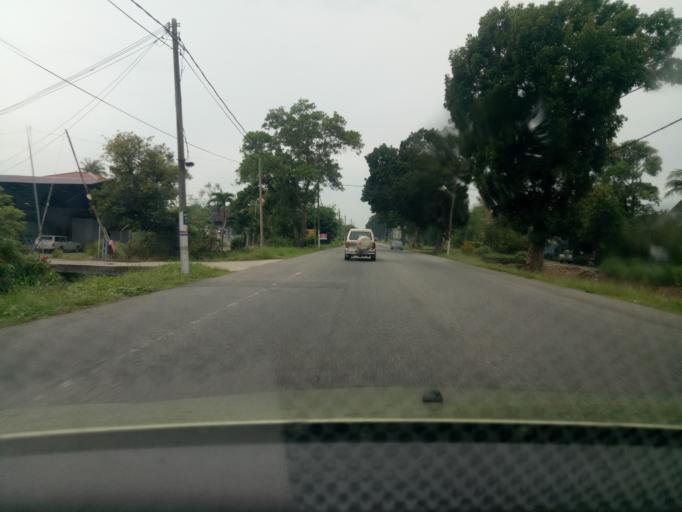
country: MY
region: Kedah
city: Gurun
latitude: 5.8946
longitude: 100.4390
